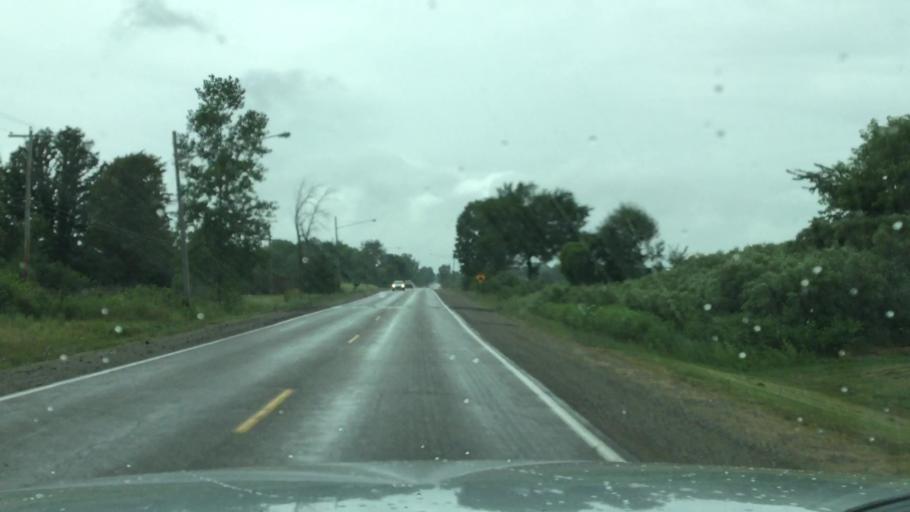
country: US
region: Michigan
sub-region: Genesee County
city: Clio
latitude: 43.1189
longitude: -83.7699
